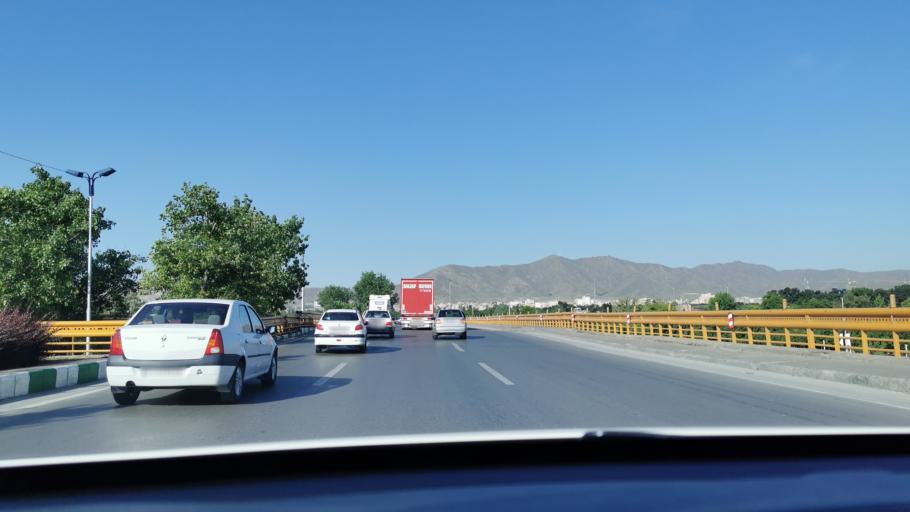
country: IR
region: Razavi Khorasan
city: Mashhad
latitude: 36.2532
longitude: 59.6150
